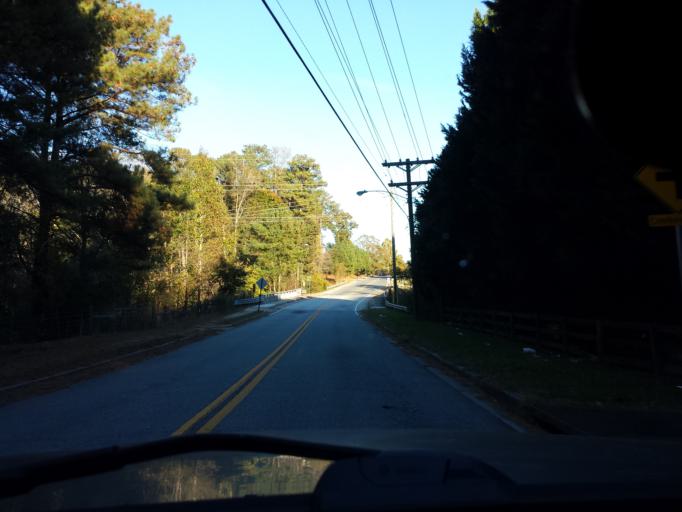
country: US
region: Georgia
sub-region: Cobb County
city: Fair Oaks
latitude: 33.8874
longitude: -84.6024
